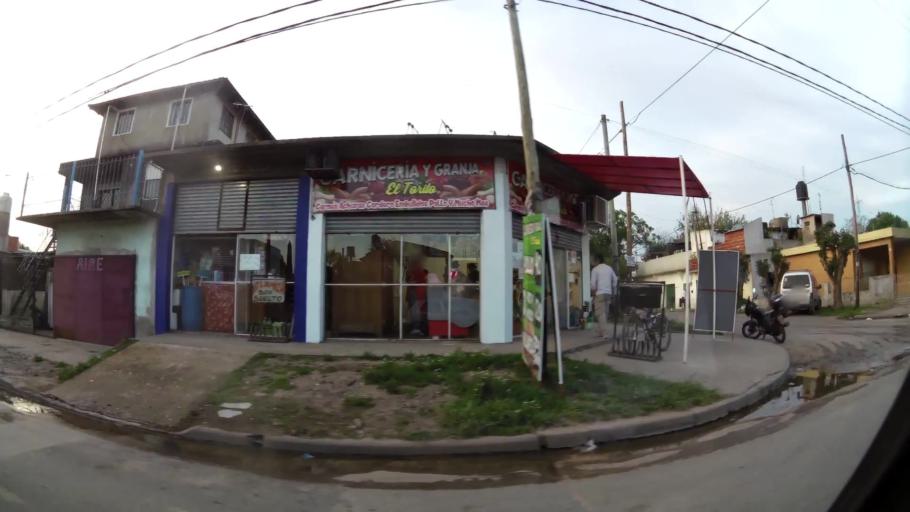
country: AR
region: Buenos Aires
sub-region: Partido de Almirante Brown
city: Adrogue
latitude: -34.8037
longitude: -58.2958
